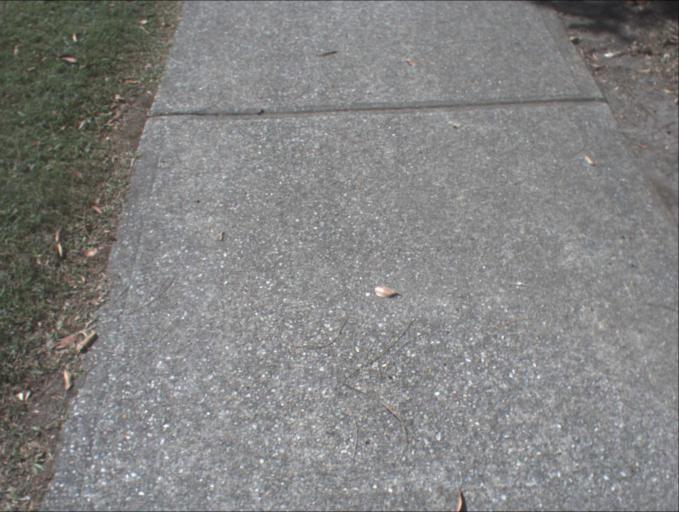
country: AU
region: Queensland
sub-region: Logan
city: Windaroo
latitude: -27.7328
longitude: 153.1928
